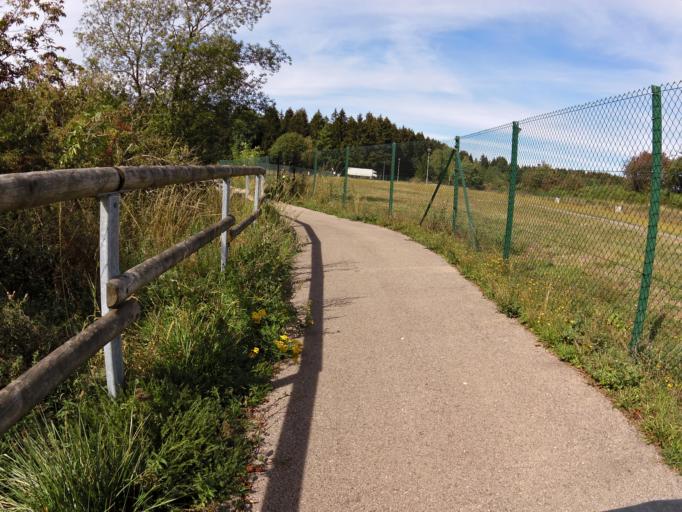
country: DE
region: Rheinland-Pfalz
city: Arzfeld
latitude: 50.0935
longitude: 6.2736
